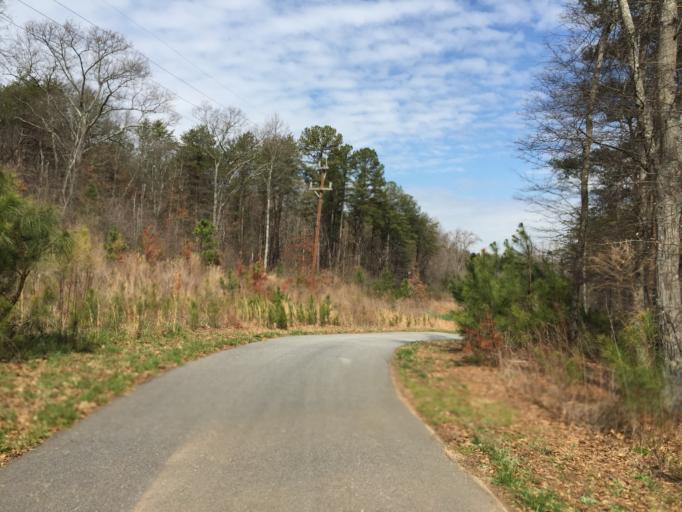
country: US
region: South Carolina
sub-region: Greenville County
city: Mauldin
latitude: 34.7852
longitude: -82.3659
